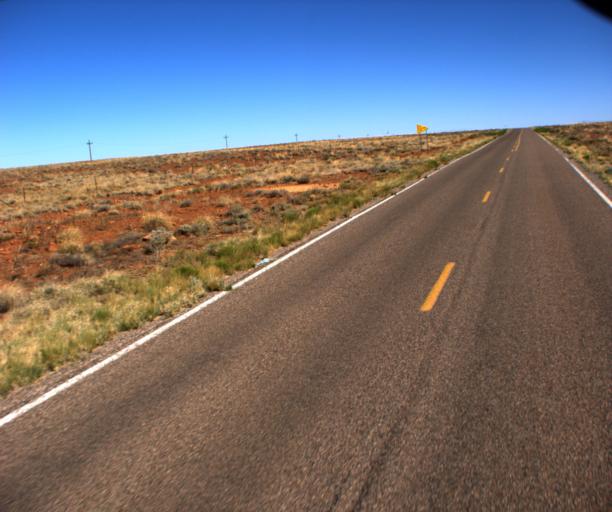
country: US
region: Arizona
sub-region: Coconino County
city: LeChee
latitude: 35.2351
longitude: -110.9585
